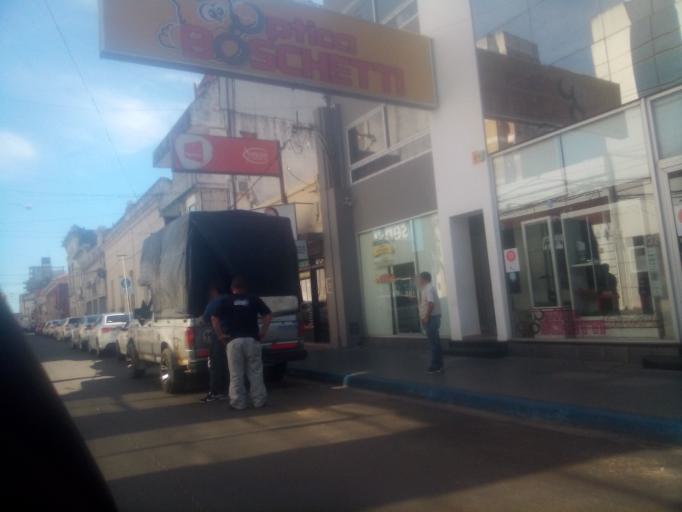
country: AR
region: Corrientes
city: Corrientes
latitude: -27.4658
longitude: -58.8342
